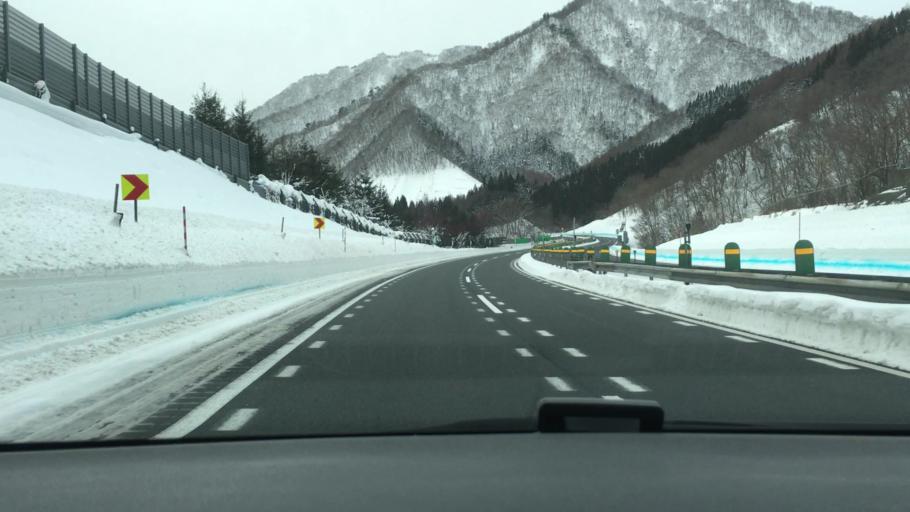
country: JP
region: Akita
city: Hanawa
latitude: 40.1313
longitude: 140.9229
